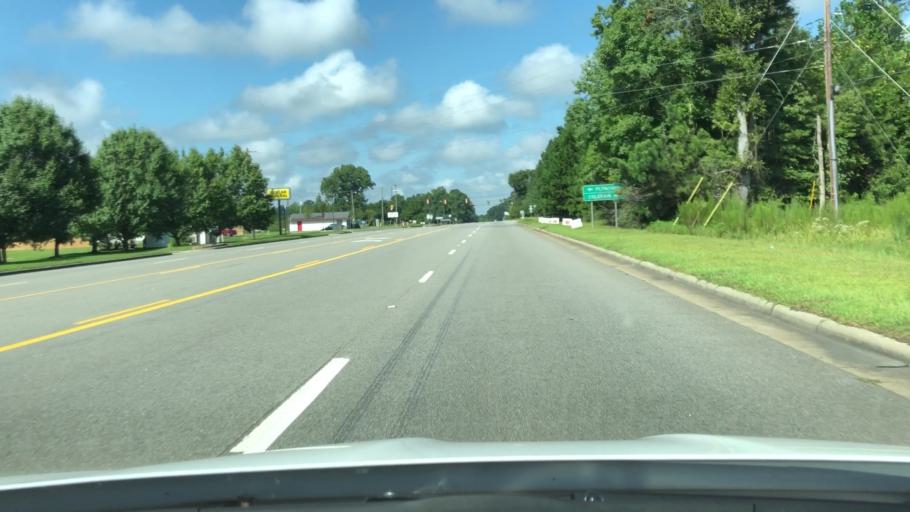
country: US
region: North Carolina
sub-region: Bertie County
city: Windsor
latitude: 36.0352
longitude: -76.7822
